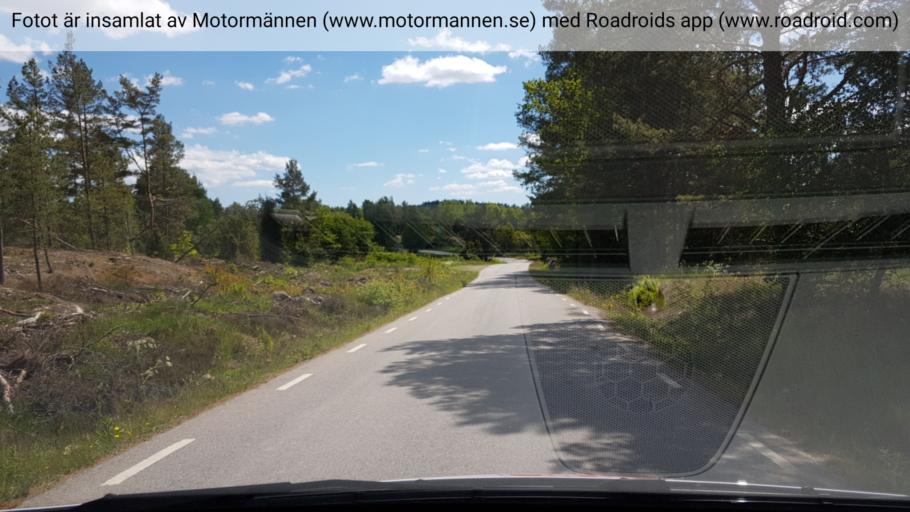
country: SE
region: Kalmar
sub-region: Vasterviks Kommun
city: Vaestervik
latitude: 57.9407
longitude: 16.6679
